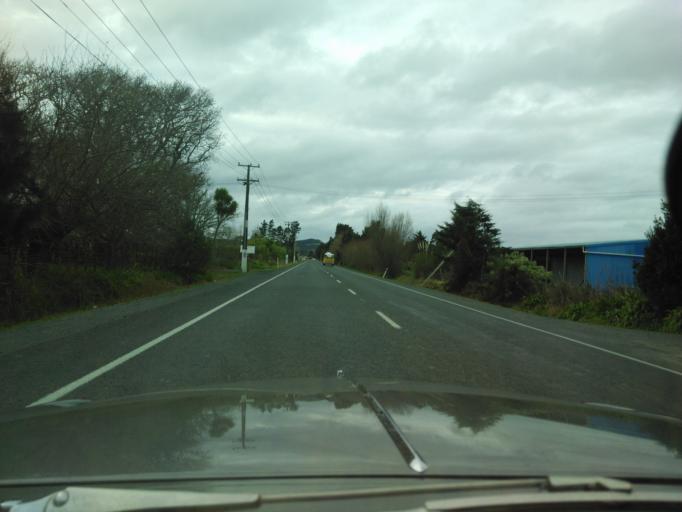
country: NZ
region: Auckland
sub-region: Auckland
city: Parakai
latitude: -36.6838
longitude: 174.4337
